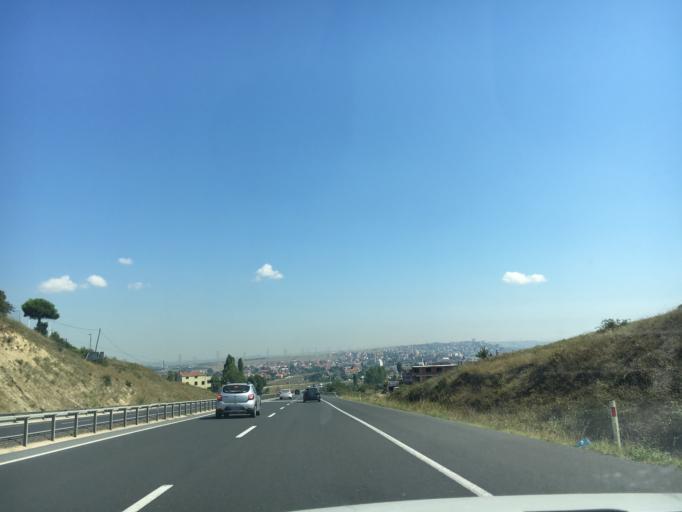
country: TR
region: Tekirdag
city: Sultankoy
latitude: 41.0022
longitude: 27.9763
